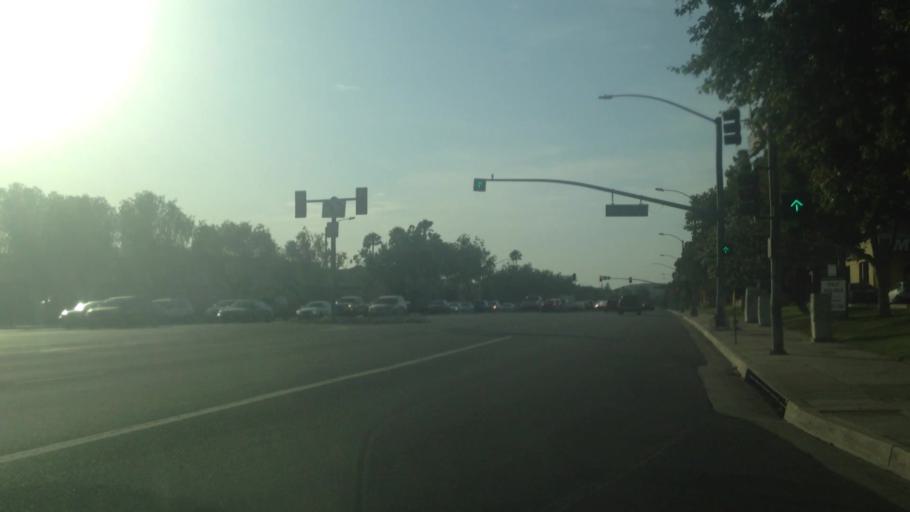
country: US
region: California
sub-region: Riverside County
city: Home Gardens
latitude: 33.8871
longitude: -117.5182
